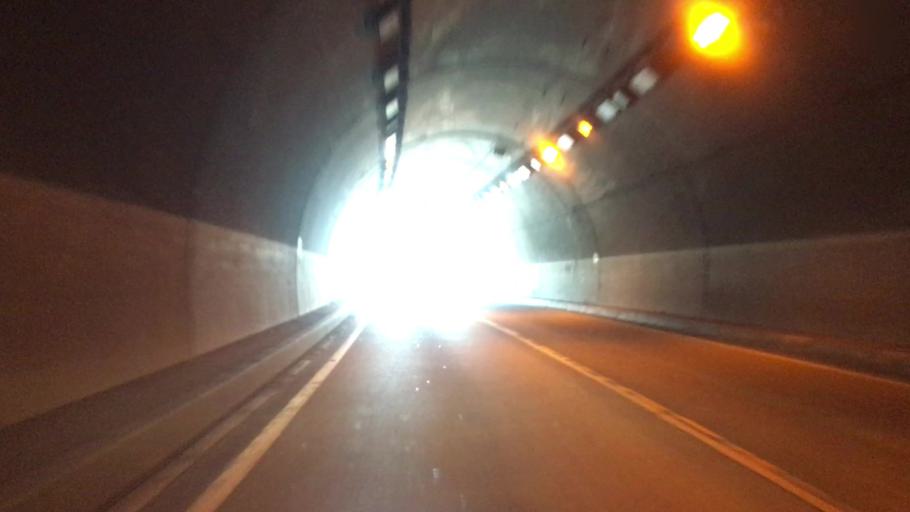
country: JP
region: Hyogo
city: Toyooka
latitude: 35.4726
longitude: 134.7711
